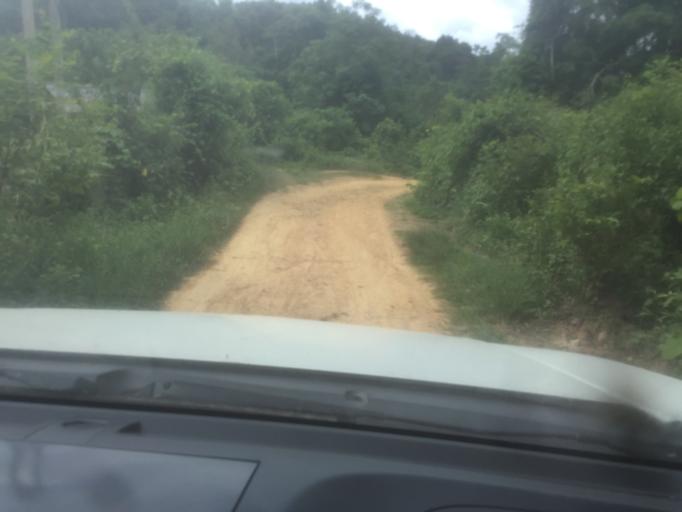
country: LA
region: Phongsali
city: Khoa
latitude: 20.9092
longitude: 102.5501
